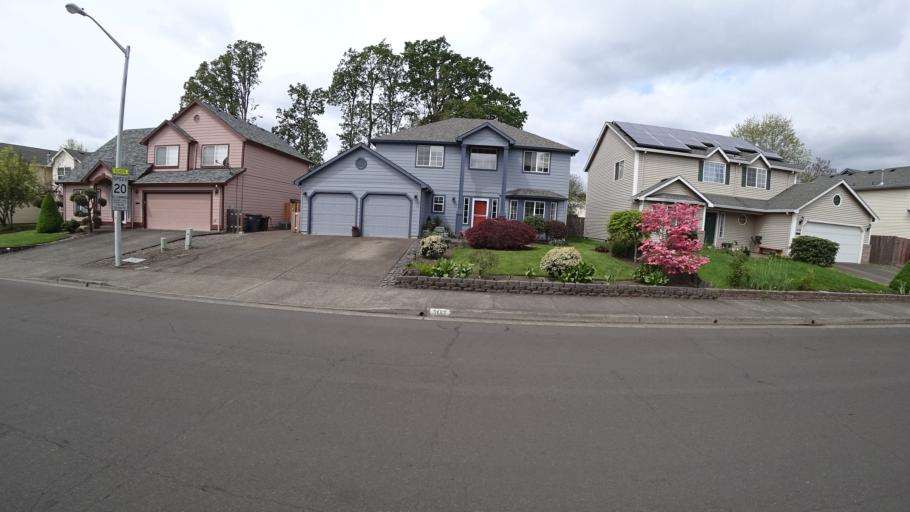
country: US
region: Oregon
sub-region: Washington County
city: Hillsboro
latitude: 45.5478
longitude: -122.9926
